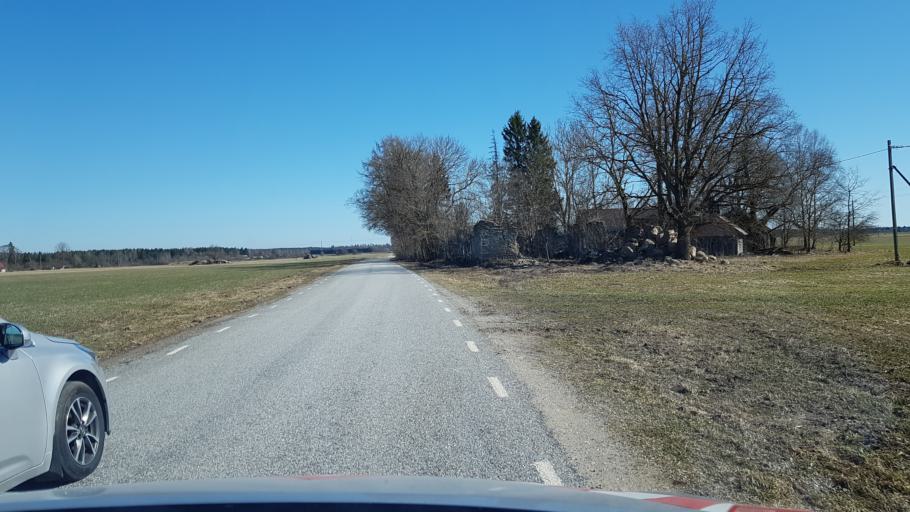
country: EE
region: Laeaene-Virumaa
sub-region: Viru-Nigula vald
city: Kunda
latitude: 59.4084
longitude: 26.5323
